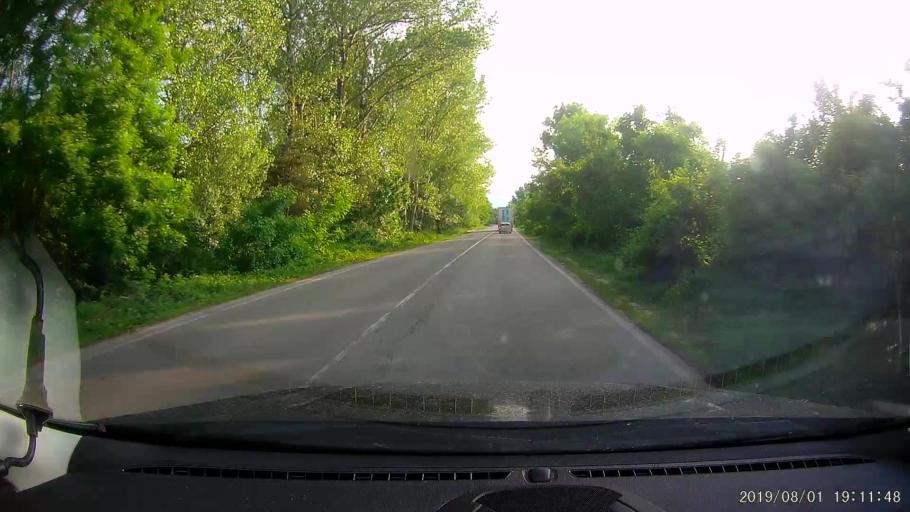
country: BG
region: Shumen
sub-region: Obshtina Smyadovo
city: Smyadovo
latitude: 42.9695
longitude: 26.9572
